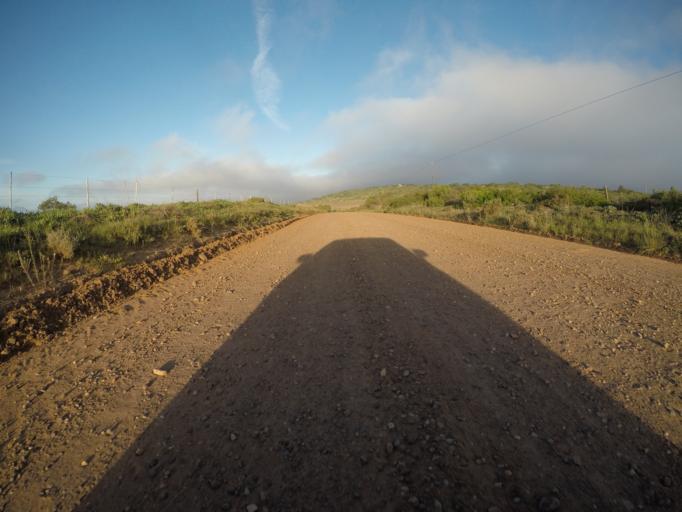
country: ZA
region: Western Cape
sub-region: Eden District Municipality
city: Mossel Bay
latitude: -34.1447
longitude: 22.0159
